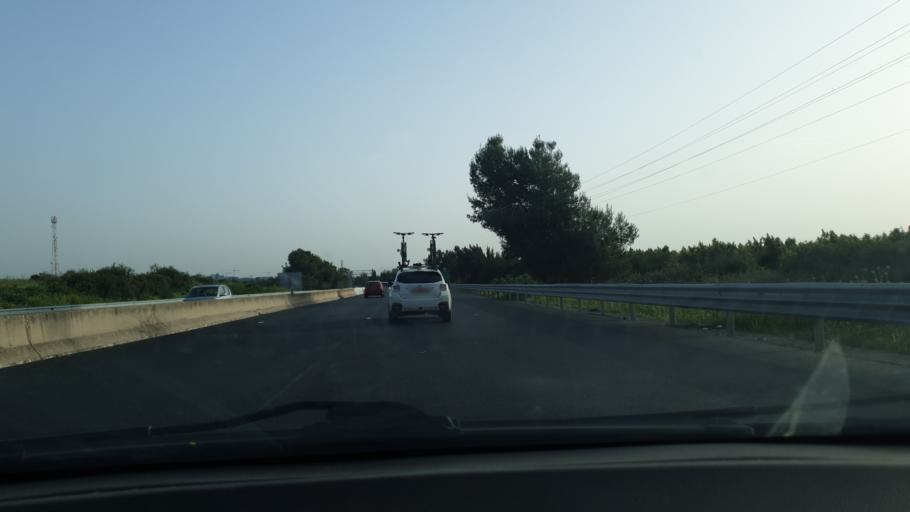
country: IL
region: Central District
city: Tel Mond
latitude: 32.2302
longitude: 34.8837
